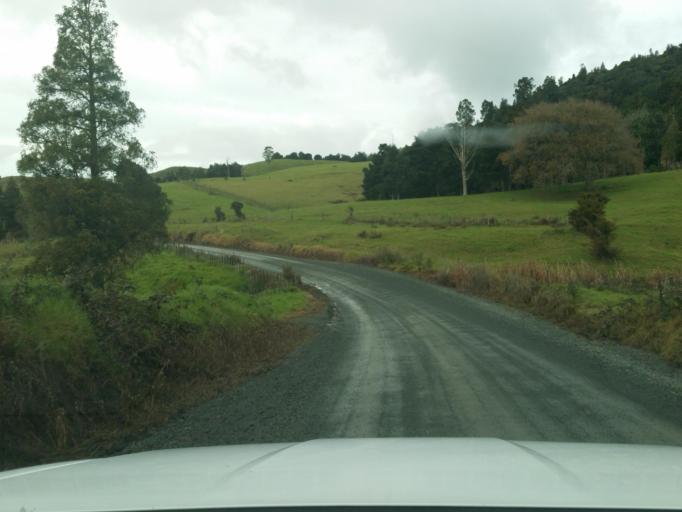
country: NZ
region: Northland
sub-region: Kaipara District
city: Dargaville
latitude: -35.8271
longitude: 173.8197
